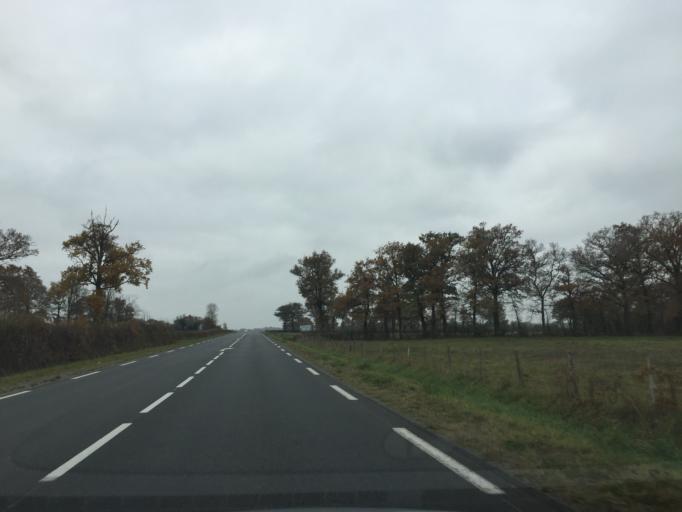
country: FR
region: Limousin
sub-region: Departement de la Creuse
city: Gouzon
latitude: 46.1615
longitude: 2.2122
